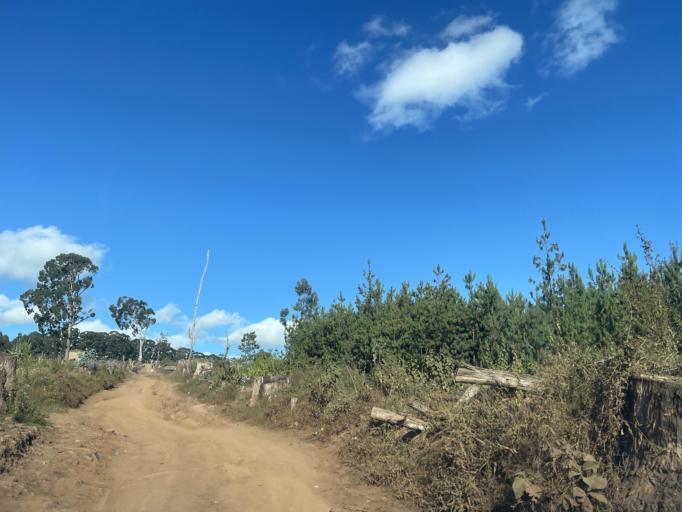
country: TZ
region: Iringa
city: Makungu
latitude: -8.5007
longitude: 35.5083
